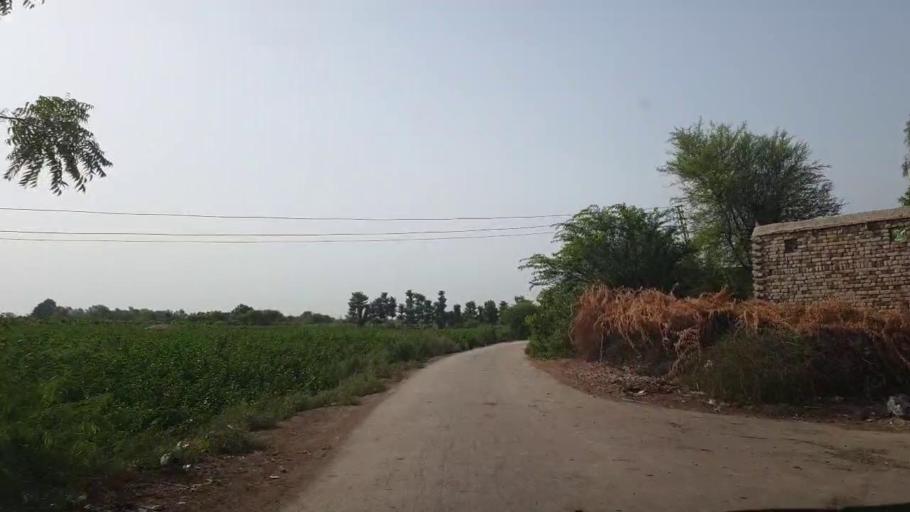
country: PK
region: Sindh
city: Nawabshah
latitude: 26.2271
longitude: 68.4221
